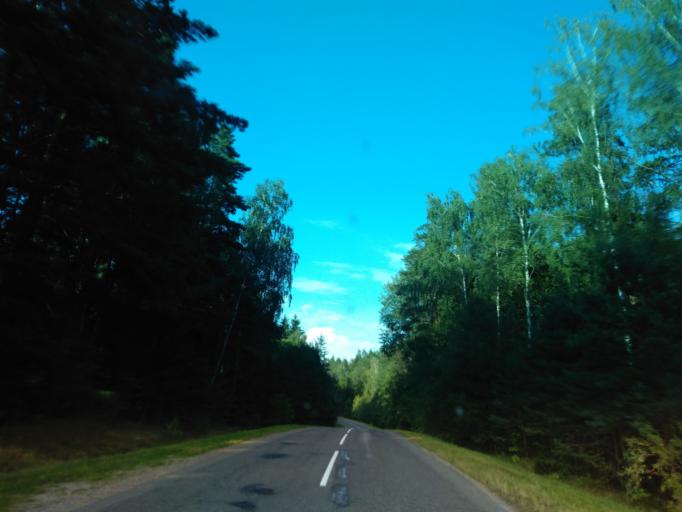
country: BY
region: Minsk
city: Kapyl'
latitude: 53.3087
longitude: 27.0820
